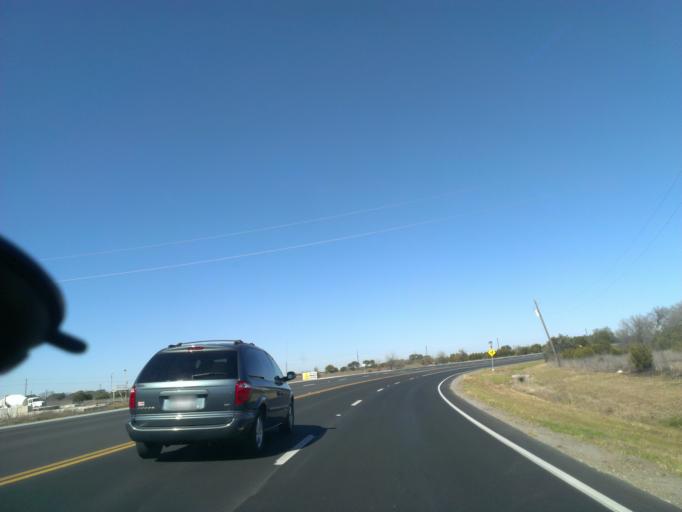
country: US
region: Texas
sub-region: Williamson County
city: Leander
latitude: 30.5969
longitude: -97.8614
